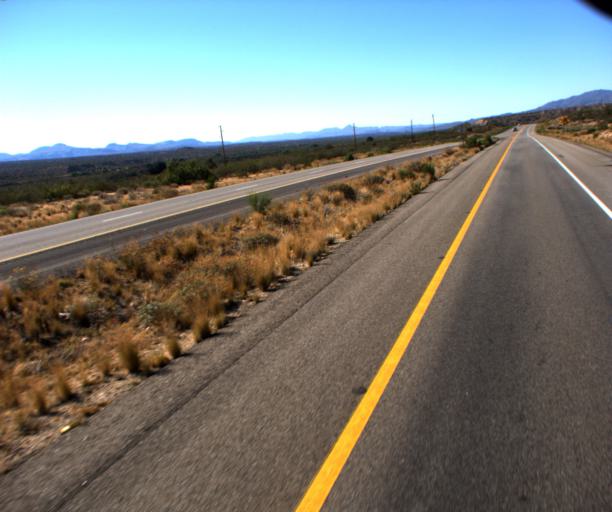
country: US
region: Arizona
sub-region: Yavapai County
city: Bagdad
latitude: 34.8138
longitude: -113.6263
